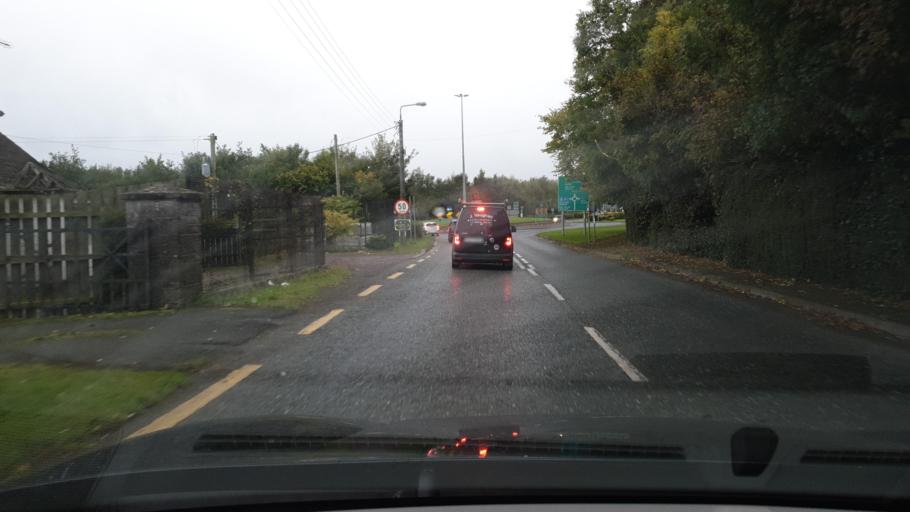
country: IE
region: Leinster
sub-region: Lu
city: Ardee
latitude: 53.8641
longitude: -6.5388
